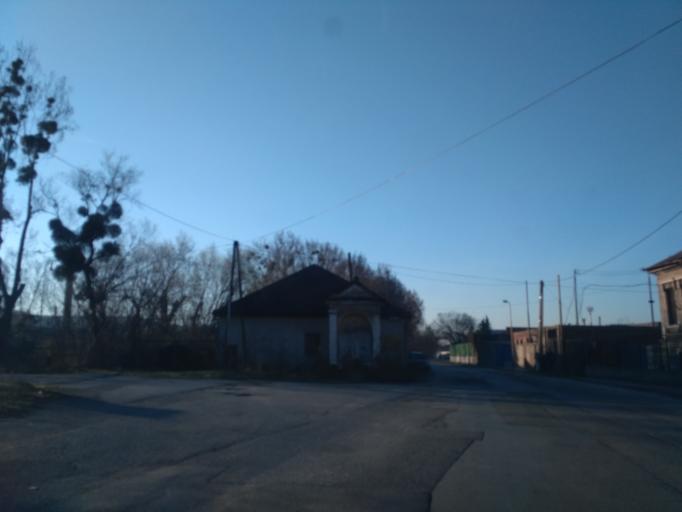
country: SK
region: Kosicky
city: Kosice
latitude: 48.7133
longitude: 21.2685
